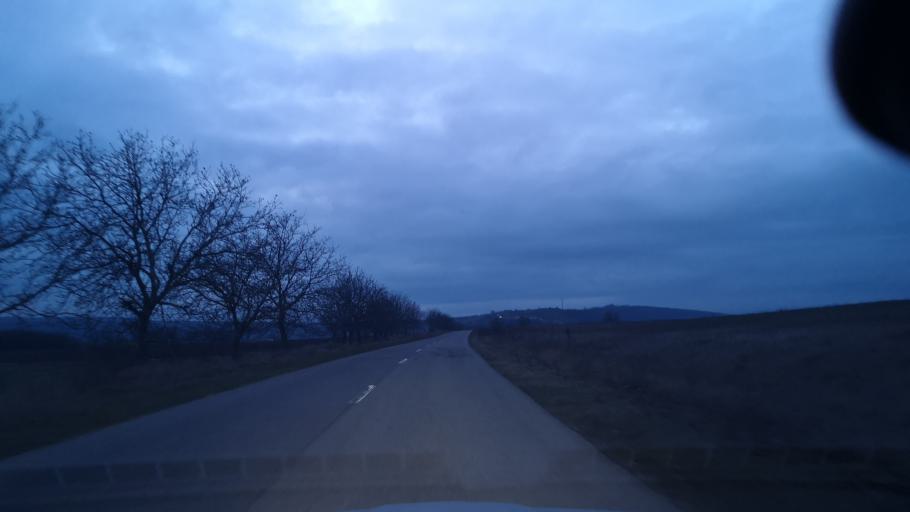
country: MD
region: Telenesti
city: Cocieri
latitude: 47.3077
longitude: 28.9813
